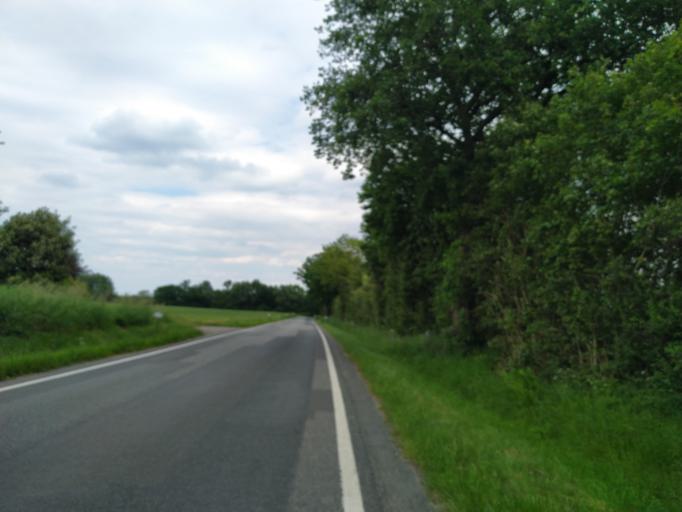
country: DE
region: Schleswig-Holstein
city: Gross Disnack
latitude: 53.7714
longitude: 10.6928
